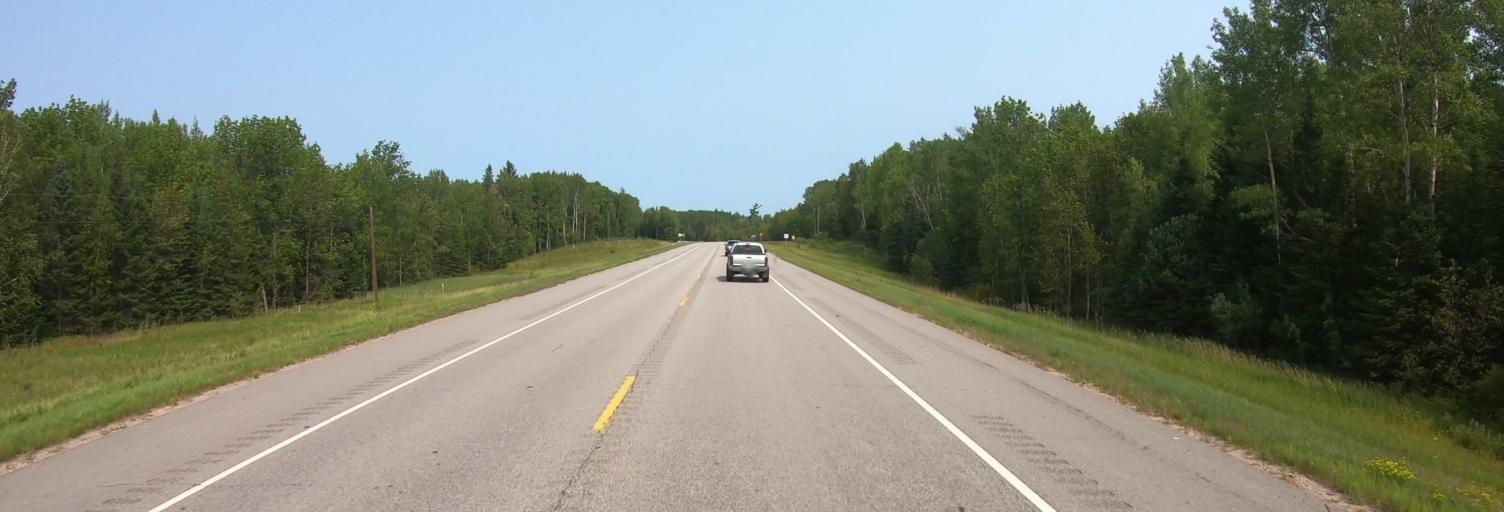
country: CA
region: Ontario
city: Fort Frances
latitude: 48.3595
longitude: -92.9632
